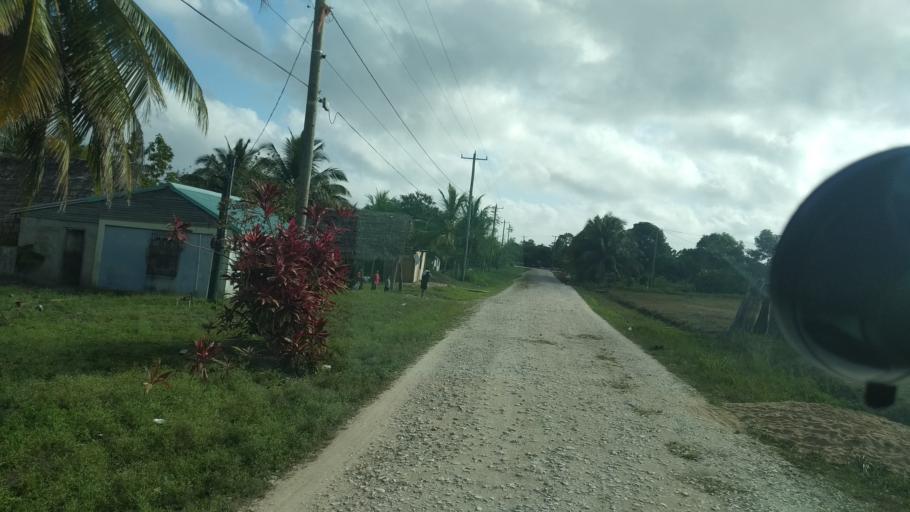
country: BZ
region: Stann Creek
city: Placencia
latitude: 16.5088
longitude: -88.5476
